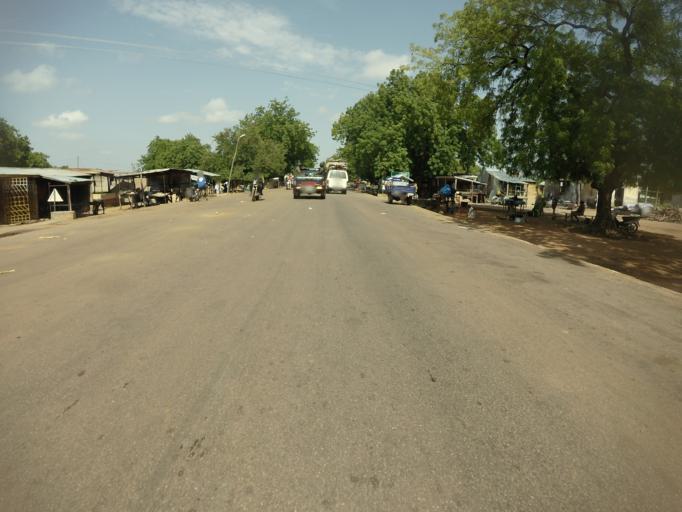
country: GH
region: Upper East
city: Bawku
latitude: 11.0682
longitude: -0.2003
